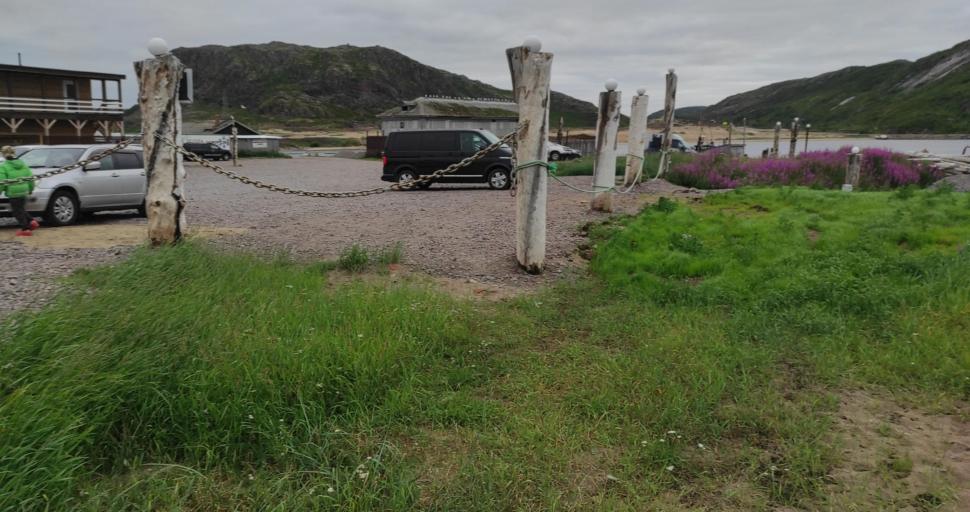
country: RU
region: Murmansk
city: Teriberka
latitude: 69.1682
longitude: 35.1318
